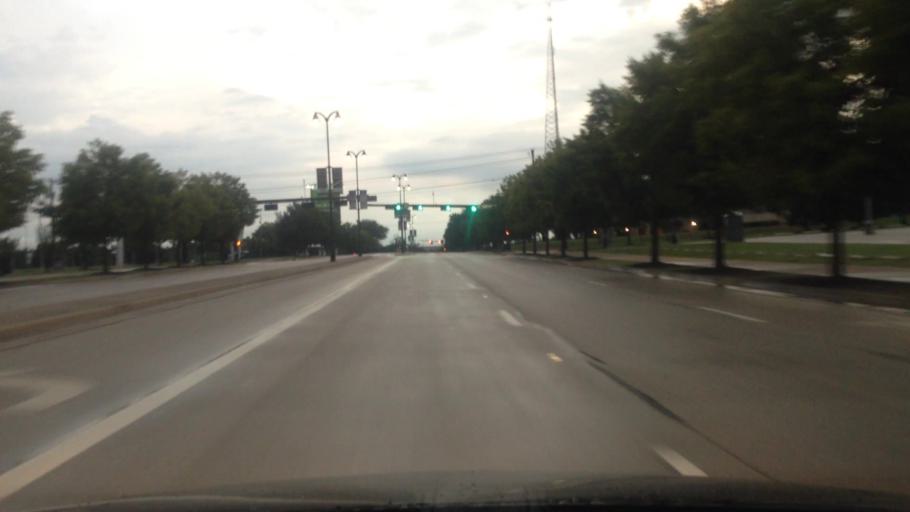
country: US
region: Texas
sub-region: Tarrant County
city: Arlington
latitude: 32.7438
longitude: -97.0908
